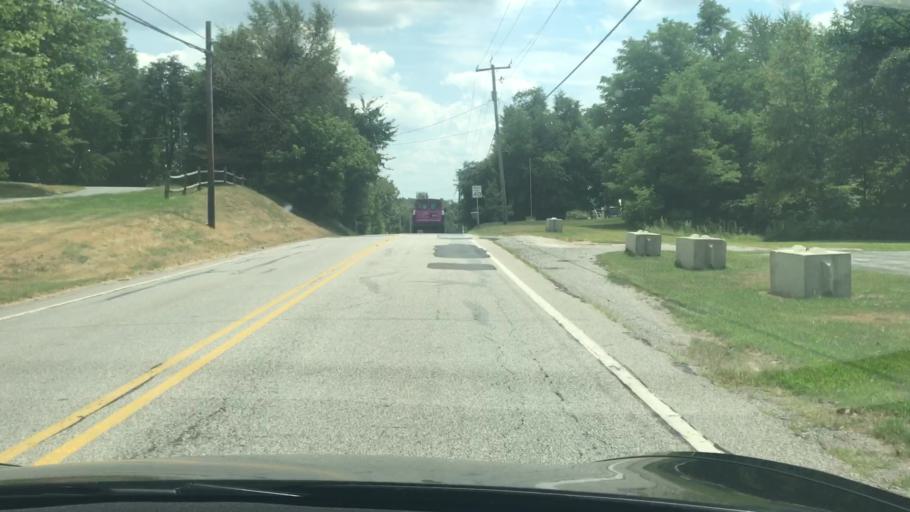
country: US
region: Pennsylvania
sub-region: York County
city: Manchester
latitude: 40.0632
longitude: -76.7665
